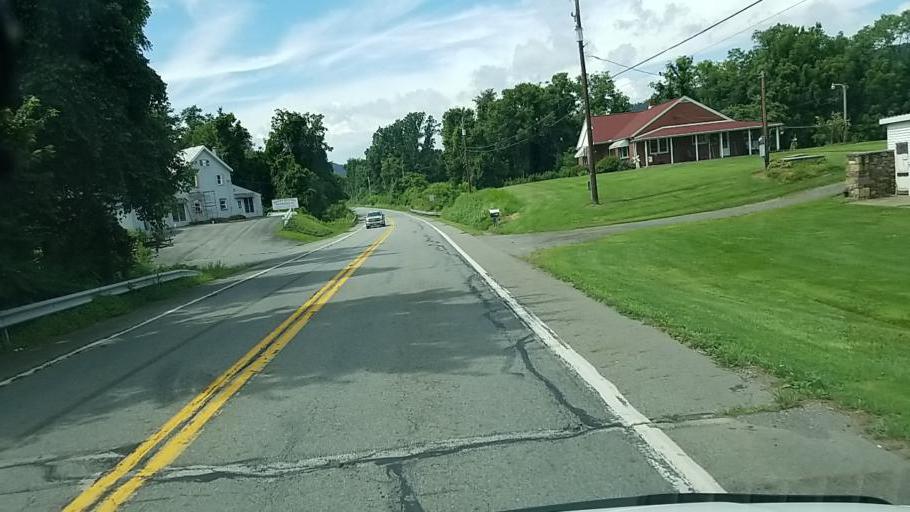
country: US
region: Pennsylvania
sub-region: Dauphin County
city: Millersburg
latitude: 40.5051
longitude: -76.9543
